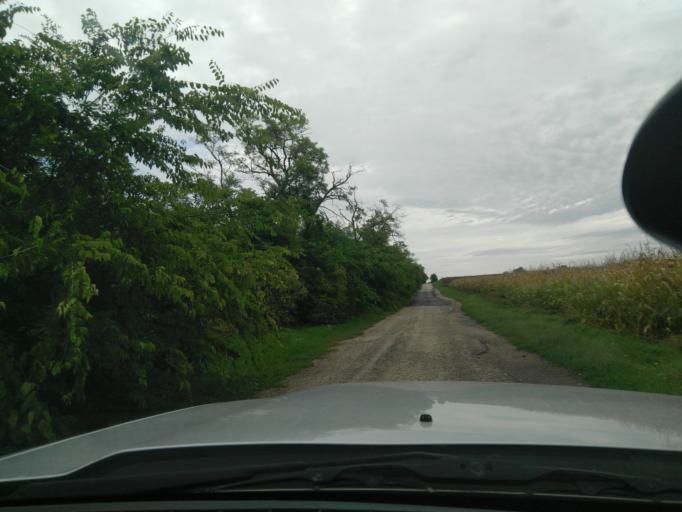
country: HU
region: Fejer
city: Martonvasar
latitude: 47.3573
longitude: 18.7828
